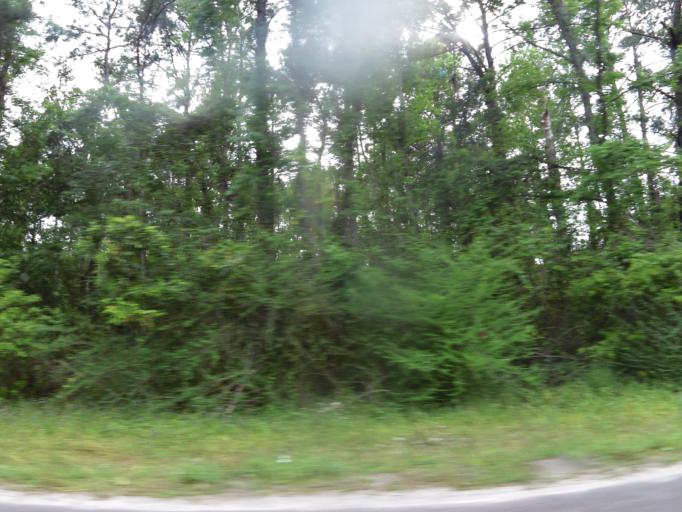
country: US
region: Florida
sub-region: Nassau County
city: Hilliard
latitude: 30.6940
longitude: -81.9247
